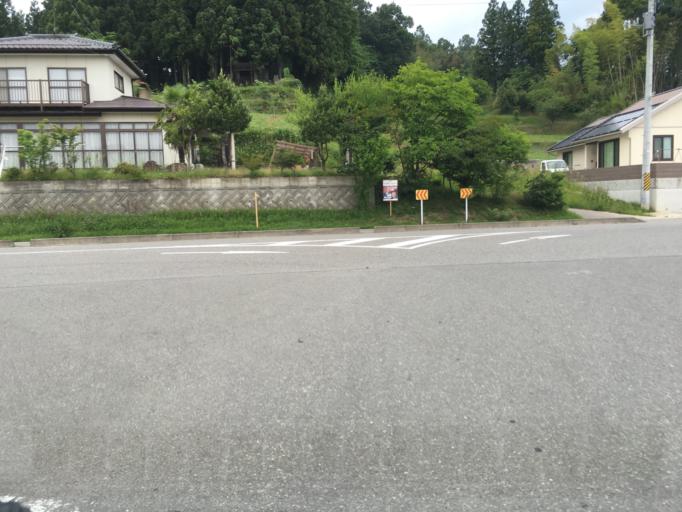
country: JP
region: Fukushima
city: Fukushima-shi
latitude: 37.6526
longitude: 140.5315
